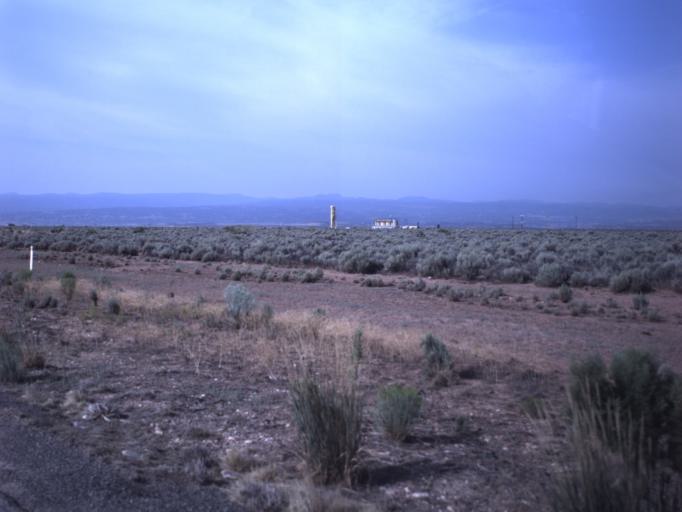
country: US
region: Utah
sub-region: Duchesne County
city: Duchesne
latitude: 40.2366
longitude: -110.3893
